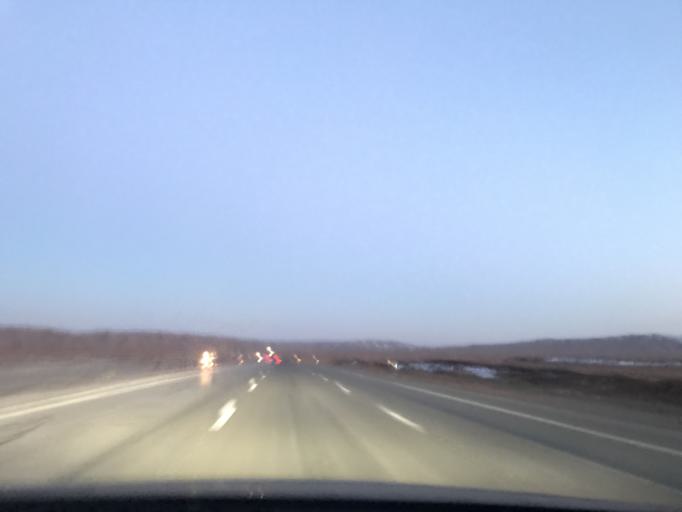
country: IR
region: Isfahan
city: Kashan
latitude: 33.8330
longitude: 51.6010
